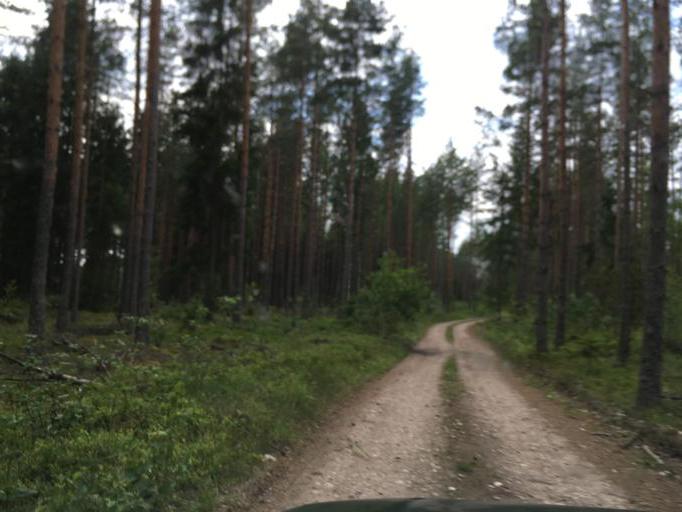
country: LV
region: Vilanu
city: Vilani
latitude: 56.7181
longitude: 26.9443
